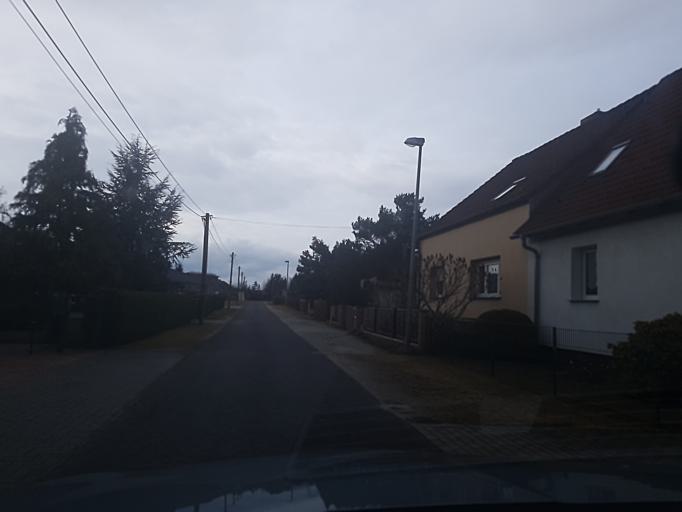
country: DE
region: Brandenburg
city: Sonnewalde
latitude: 51.6853
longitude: 13.6500
